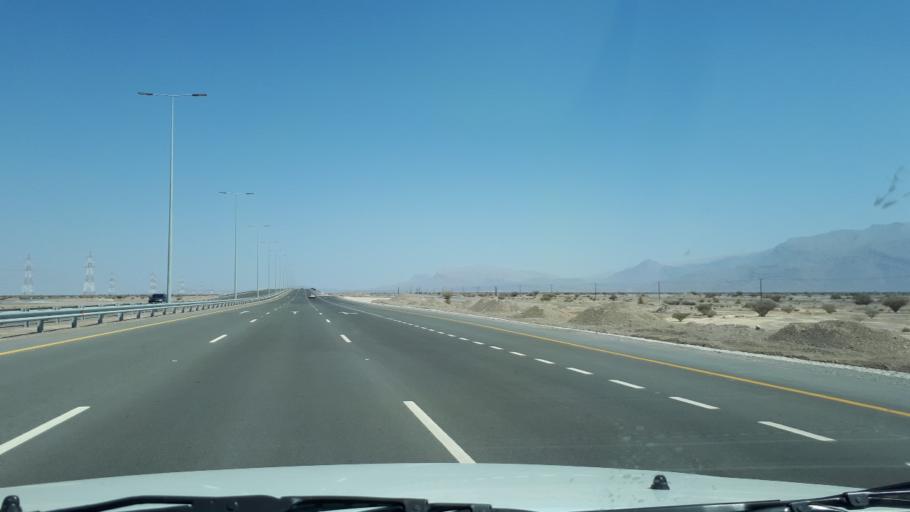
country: OM
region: Ash Sharqiyah
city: Badiyah
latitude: 22.3152
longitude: 59.1386
